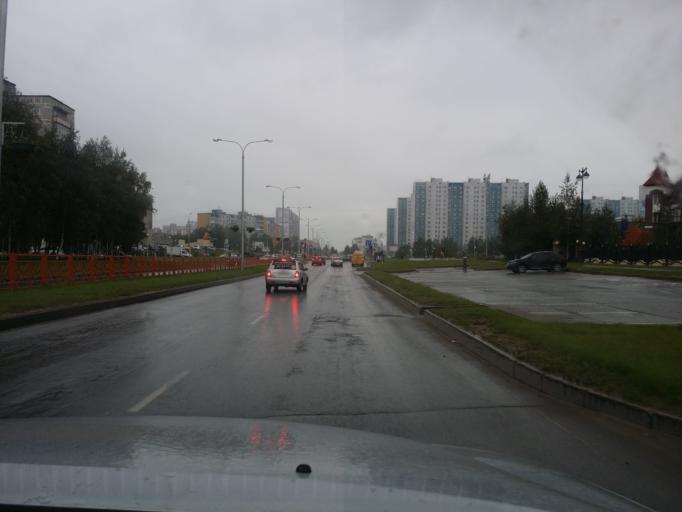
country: RU
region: Khanty-Mansiyskiy Avtonomnyy Okrug
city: Nizhnevartovsk
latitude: 60.9418
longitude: 76.5980
